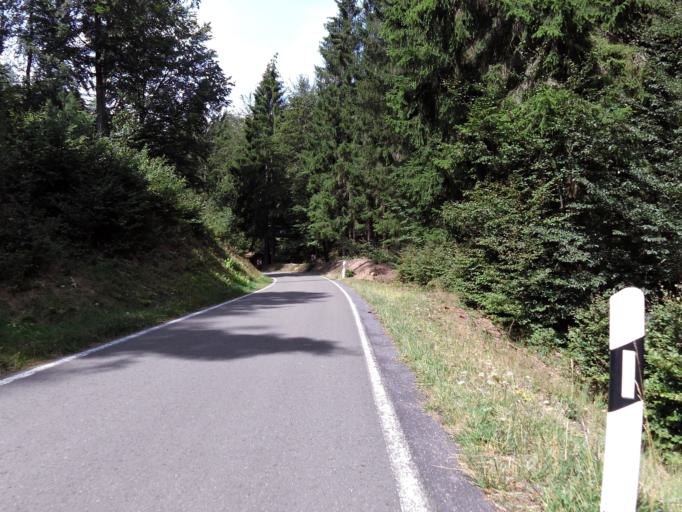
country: DE
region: Rheinland-Pfalz
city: Elmstein
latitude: 49.3861
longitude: 7.9367
